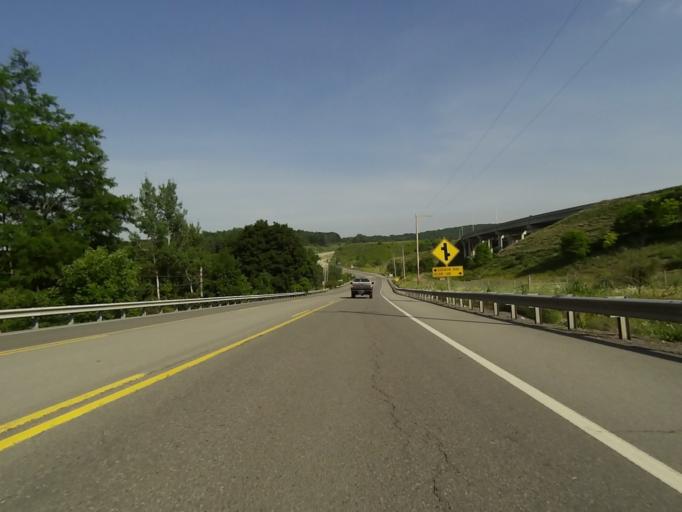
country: US
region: Pennsylvania
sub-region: Centre County
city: Park Forest Village
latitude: 40.8249
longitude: -77.9473
